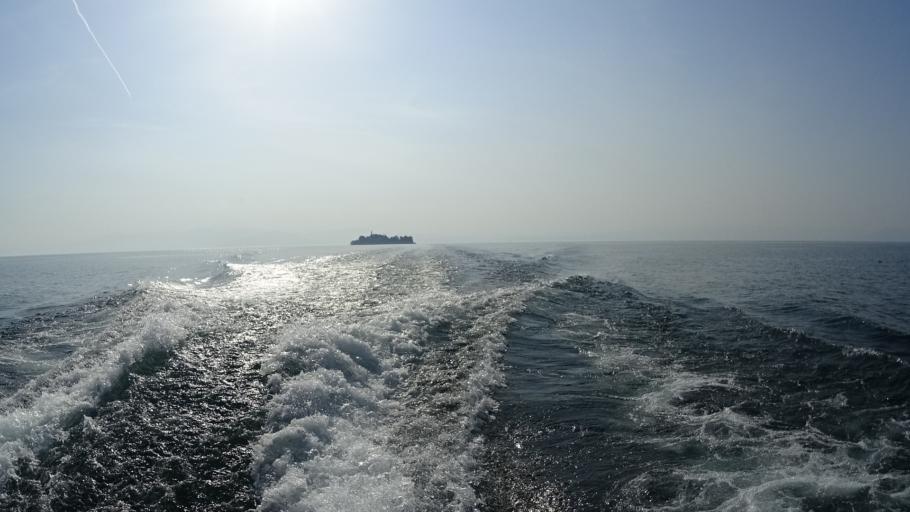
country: JP
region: Shiga Prefecture
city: Hikone
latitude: 35.2946
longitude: 136.1930
